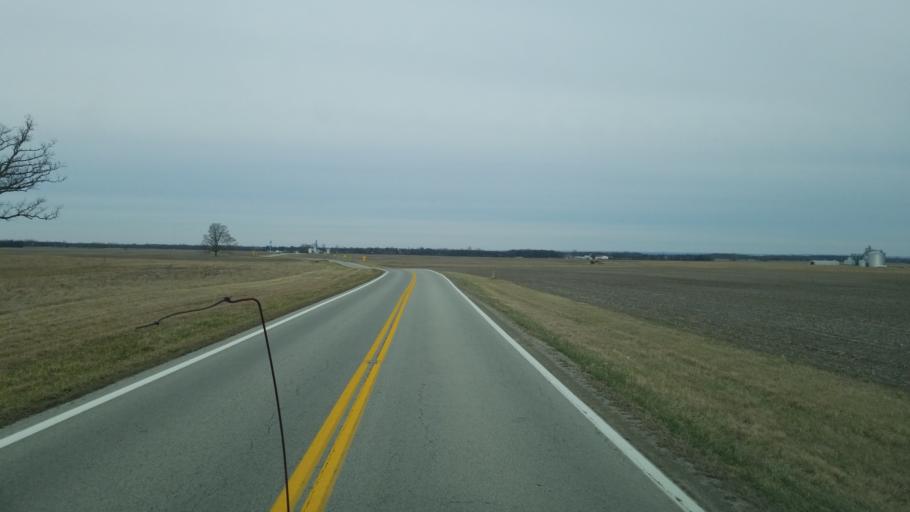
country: US
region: Ohio
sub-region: Ross County
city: Frankfort
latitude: 39.4886
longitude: -83.1754
